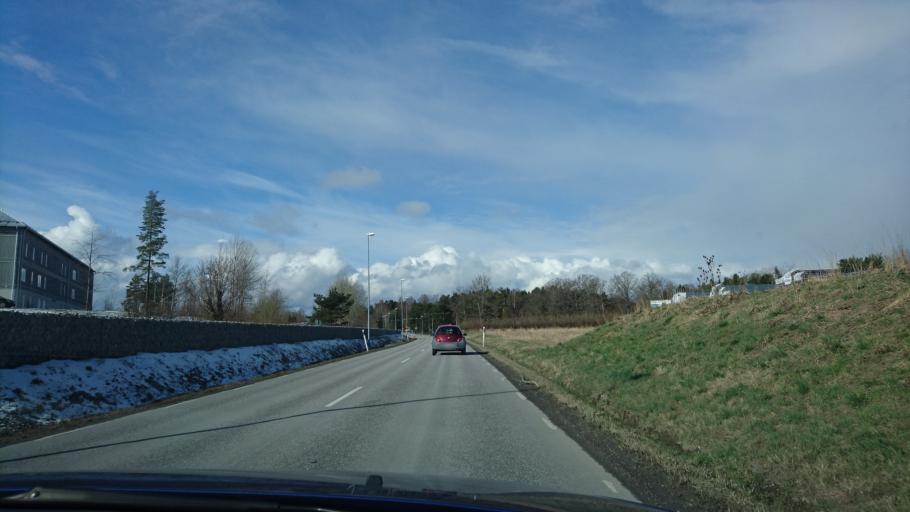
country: SE
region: Stockholm
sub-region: Norrtalje Kommun
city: Norrtalje
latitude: 59.7712
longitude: 18.7347
